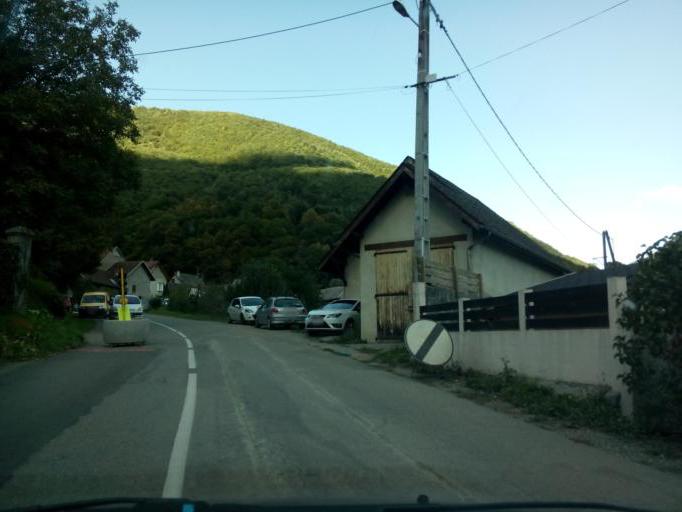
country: FR
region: Rhone-Alpes
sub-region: Departement de l'Isere
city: Vaulnaveys-le-Bas
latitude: 45.0447
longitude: 5.8287
